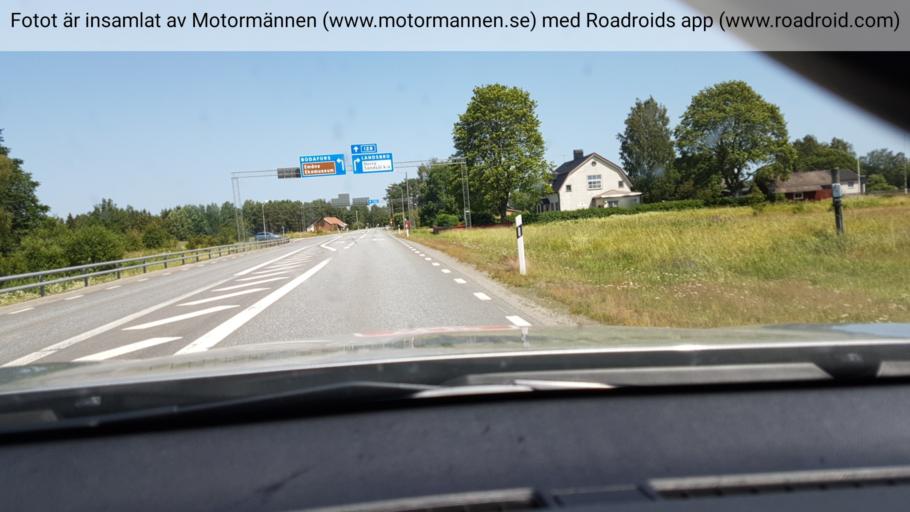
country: SE
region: Joenkoeping
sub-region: Nassjo Kommun
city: Bodafors
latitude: 57.4658
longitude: 14.7566
